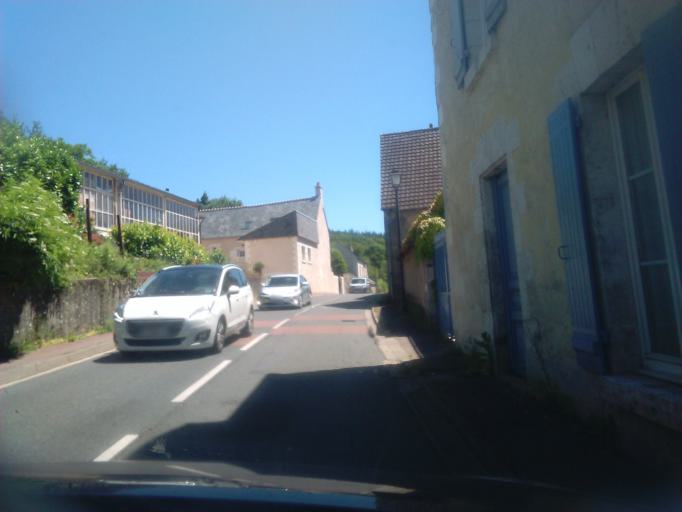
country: FR
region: Centre
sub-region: Departement du Loir-et-Cher
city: Saint-Sulpice-de-Pommeray
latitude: 47.5781
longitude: 1.2161
